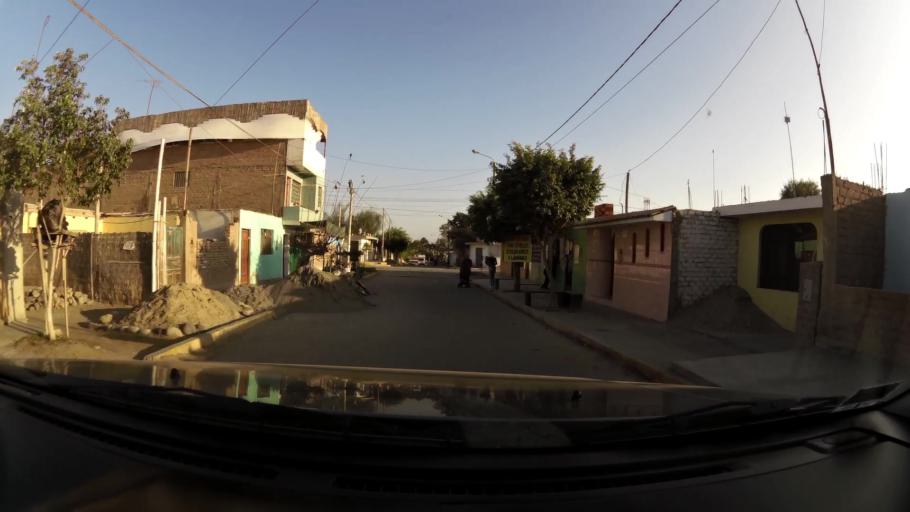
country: PE
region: Ica
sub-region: Provincia de Pisco
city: Villa Tupac Amaru
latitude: -13.7159
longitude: -76.1517
